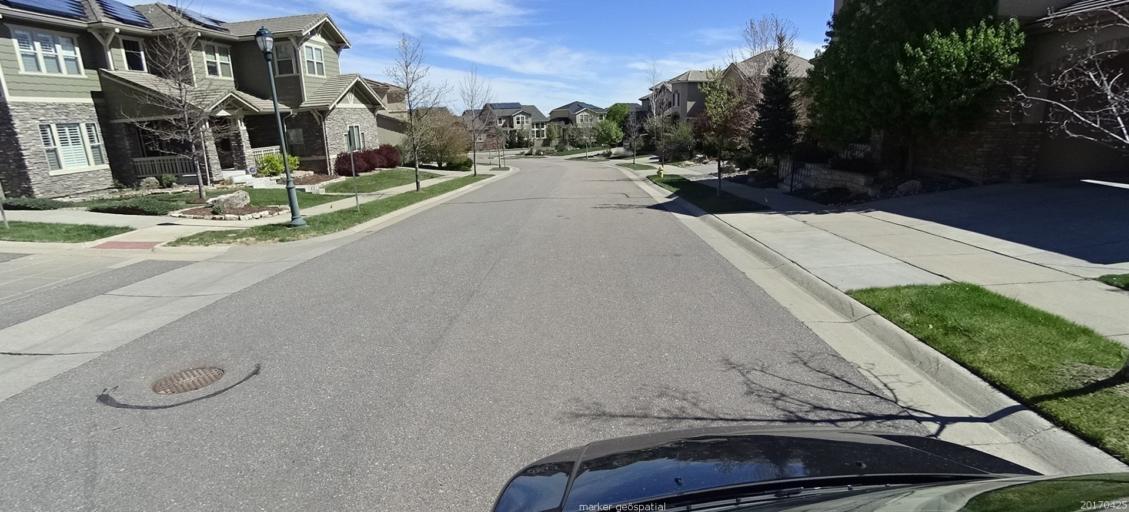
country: US
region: Colorado
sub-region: Douglas County
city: Carriage Club
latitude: 39.5259
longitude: -104.8834
